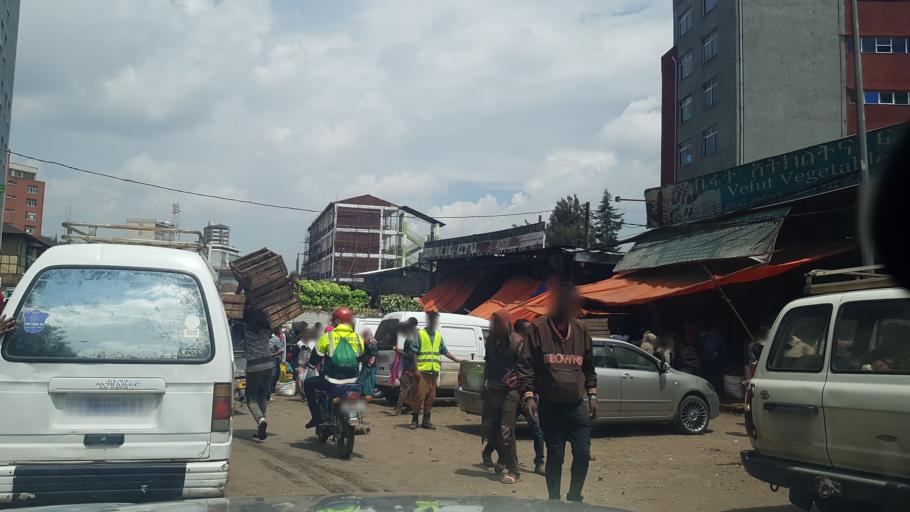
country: ET
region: Adis Abeba
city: Addis Ababa
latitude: 9.0343
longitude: 38.7473
